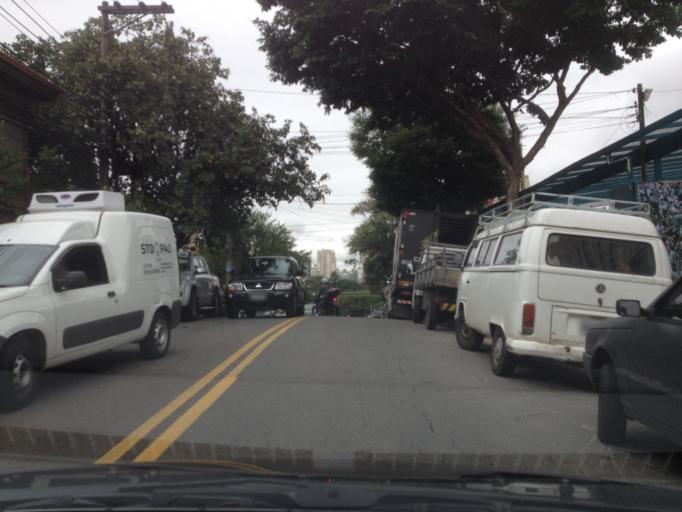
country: BR
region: Sao Paulo
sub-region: Sao Paulo
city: Sao Paulo
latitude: -23.5559
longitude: -46.6888
